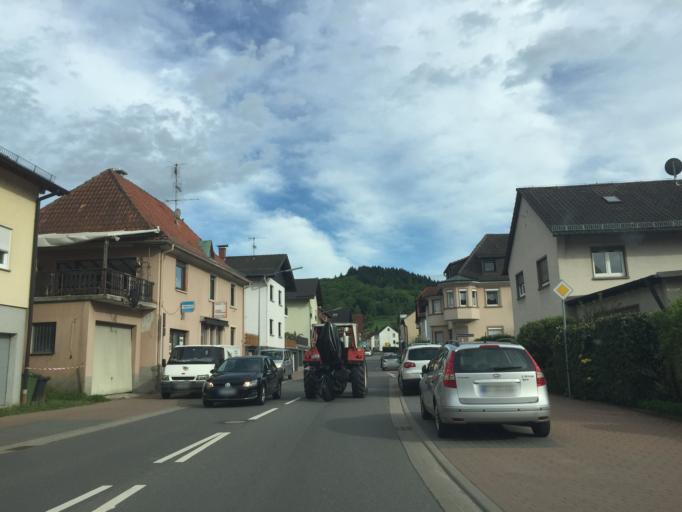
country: DE
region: Hesse
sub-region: Regierungsbezirk Darmstadt
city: Birkenau
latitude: 49.5331
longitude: 8.7275
